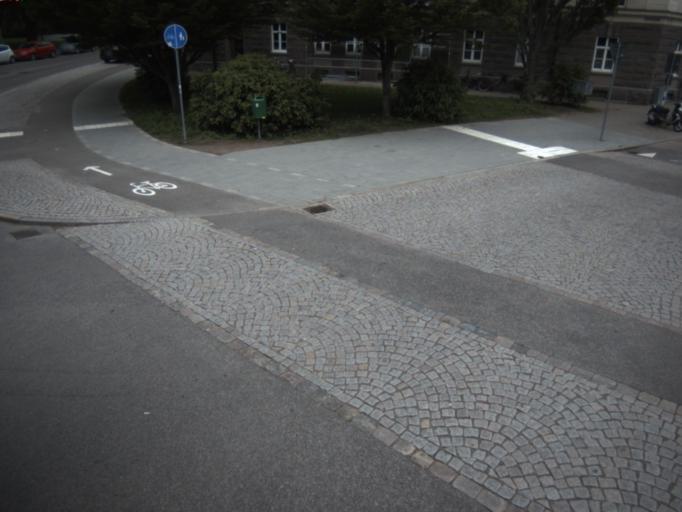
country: SE
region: Skane
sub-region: Helsingborg
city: Helsingborg
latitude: 56.0548
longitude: 12.6955
